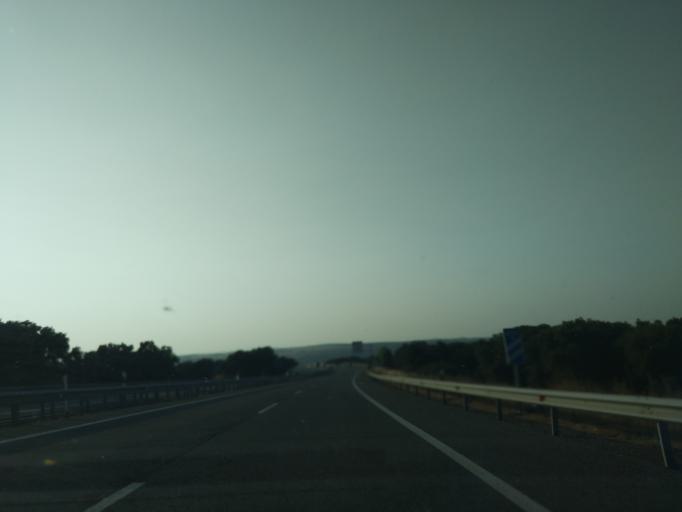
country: ES
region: Castille and Leon
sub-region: Provincia de Avila
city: Avila
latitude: 40.6734
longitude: -4.6789
